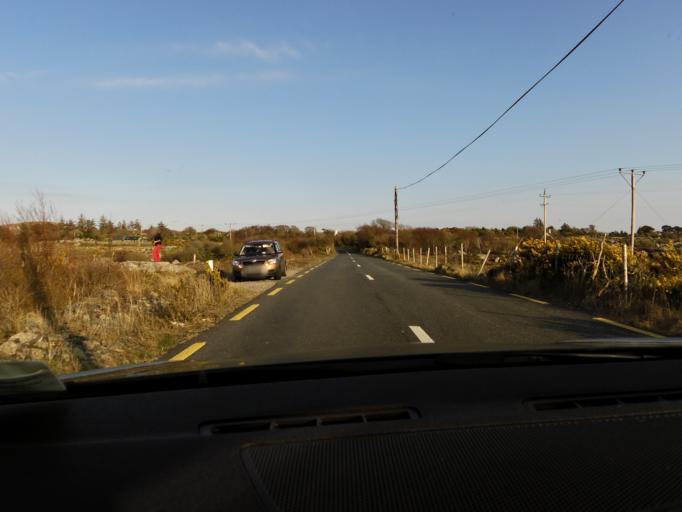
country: IE
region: Connaught
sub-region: County Galway
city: Oughterard
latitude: 53.3904
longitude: -9.6353
